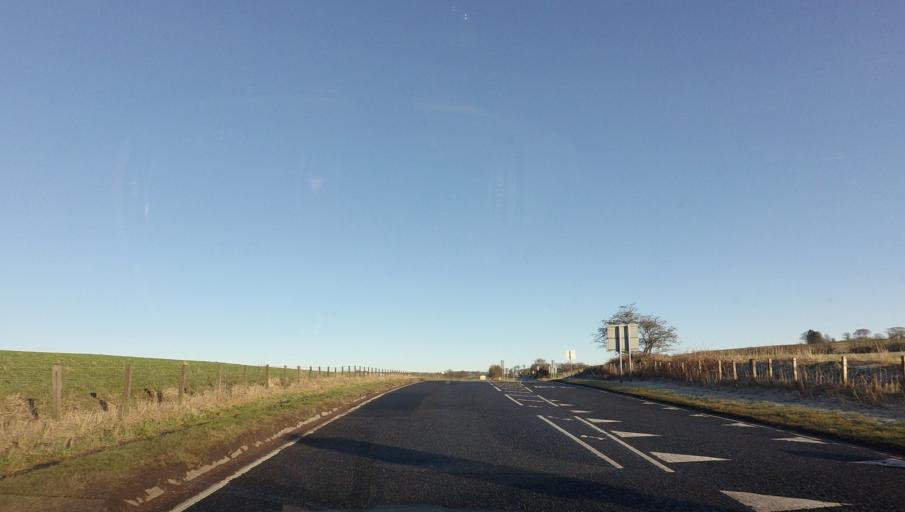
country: GB
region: Scotland
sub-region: North Lanarkshire
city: Shotts
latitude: 55.8031
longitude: -3.8236
